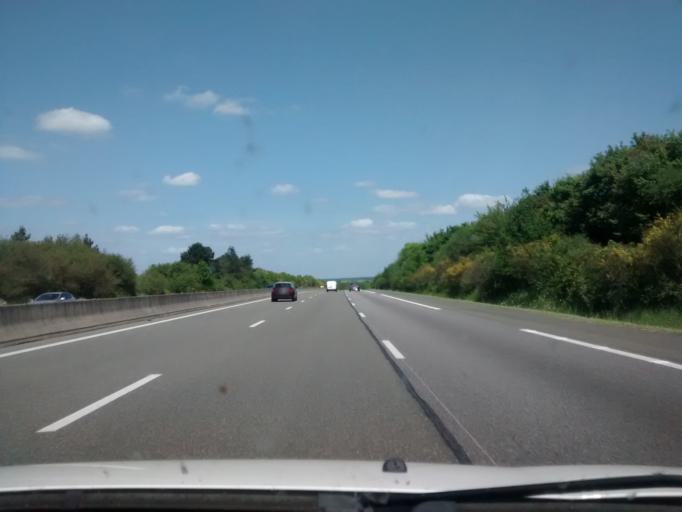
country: FR
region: Centre
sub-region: Departement d'Eure-et-Loir
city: Gallardon
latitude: 48.5011
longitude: 1.6965
